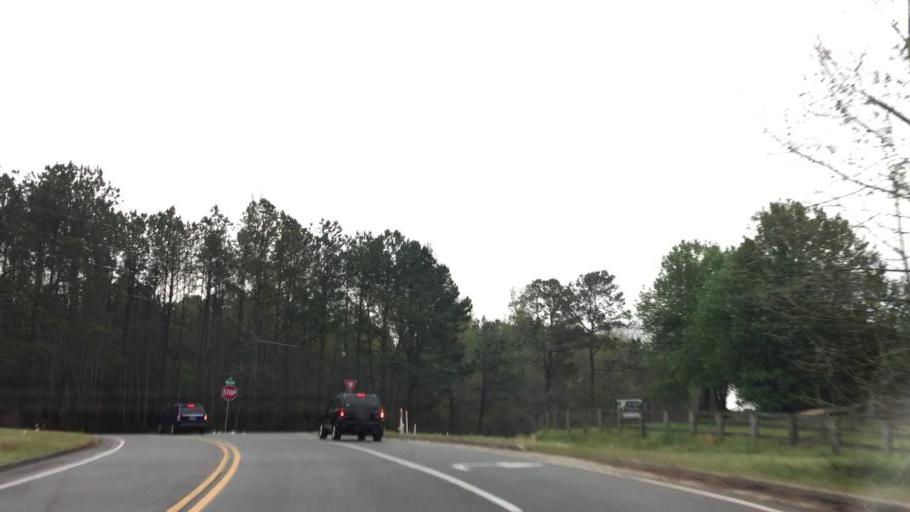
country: US
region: Georgia
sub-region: Fulton County
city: Milton
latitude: 34.1938
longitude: -84.3071
